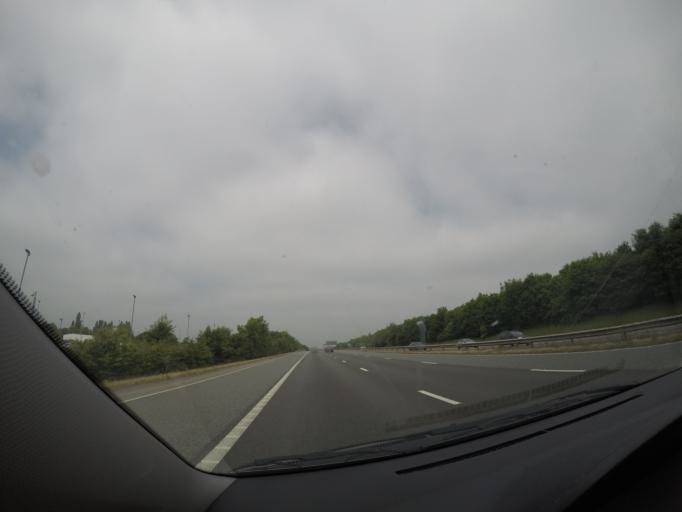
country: GB
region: England
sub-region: North Yorkshire
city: Boroughbridge
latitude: 54.0900
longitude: -1.4044
